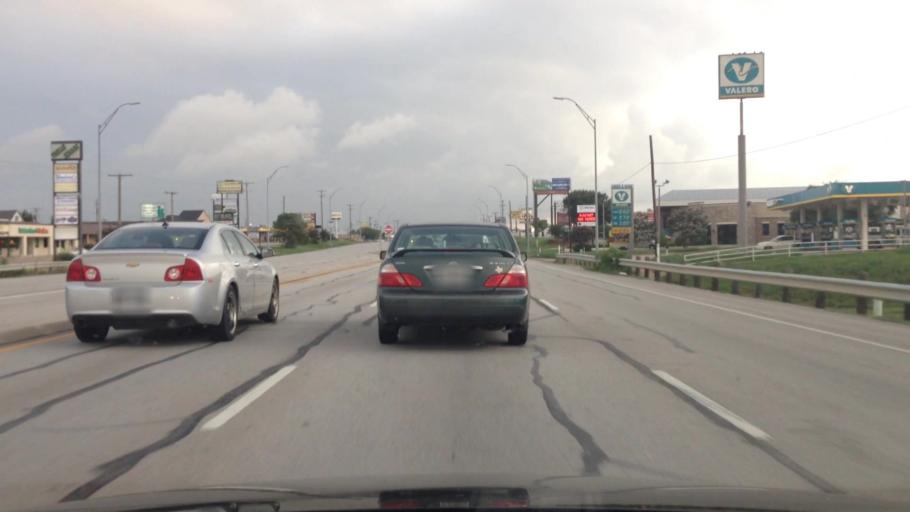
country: US
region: Texas
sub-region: Johnson County
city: Burleson
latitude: 32.5393
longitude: -97.3325
